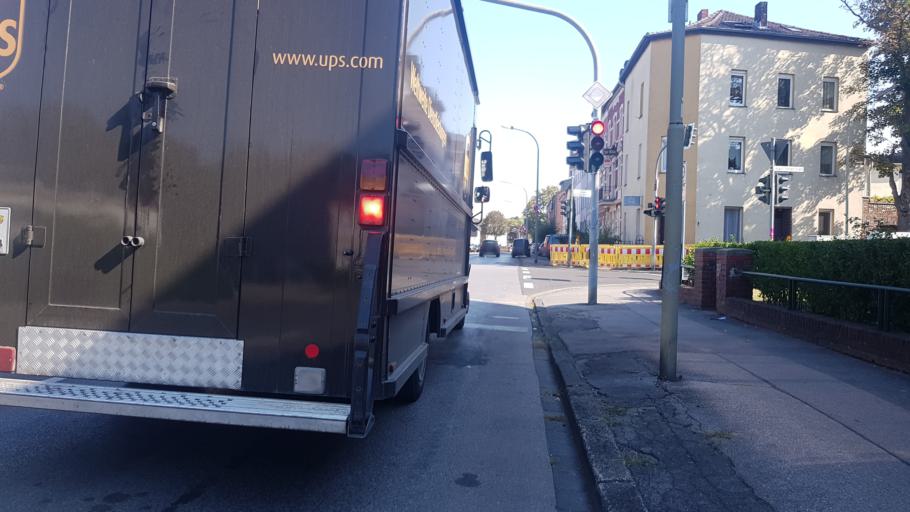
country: DE
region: North Rhine-Westphalia
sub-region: Regierungsbezirk Koln
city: Eschweiler
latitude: 50.8191
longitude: 6.2538
